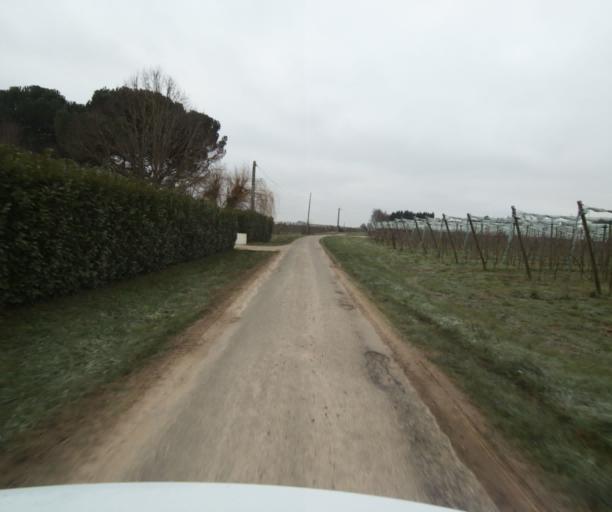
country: FR
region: Midi-Pyrenees
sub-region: Departement du Tarn-et-Garonne
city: Moissac
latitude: 44.1045
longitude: 1.1438
